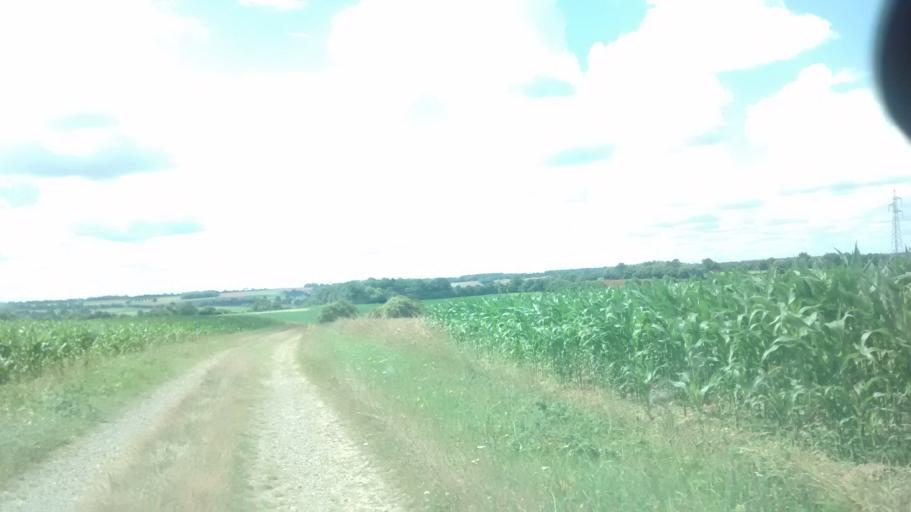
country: FR
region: Brittany
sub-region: Departement d'Ille-et-Vilaine
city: Grand-Fougeray
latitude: 47.7694
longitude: -1.7533
